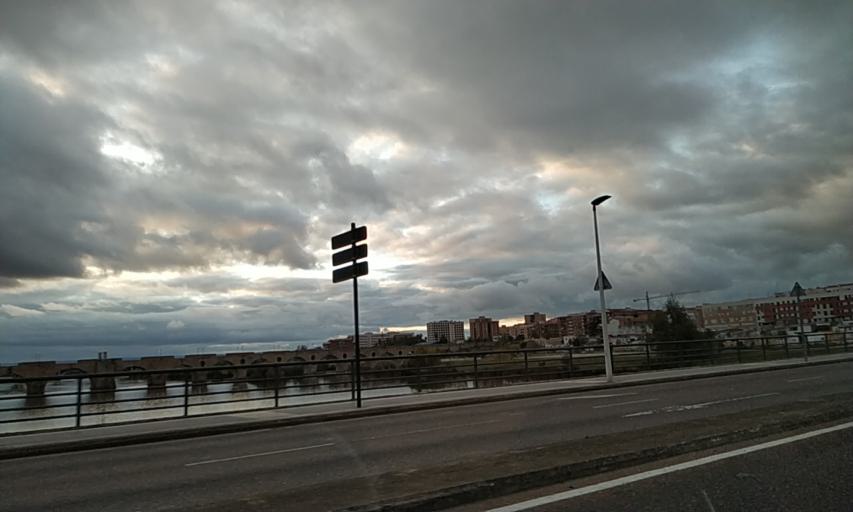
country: ES
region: Extremadura
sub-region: Provincia de Badajoz
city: Badajoz
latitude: 38.8837
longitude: -6.9733
